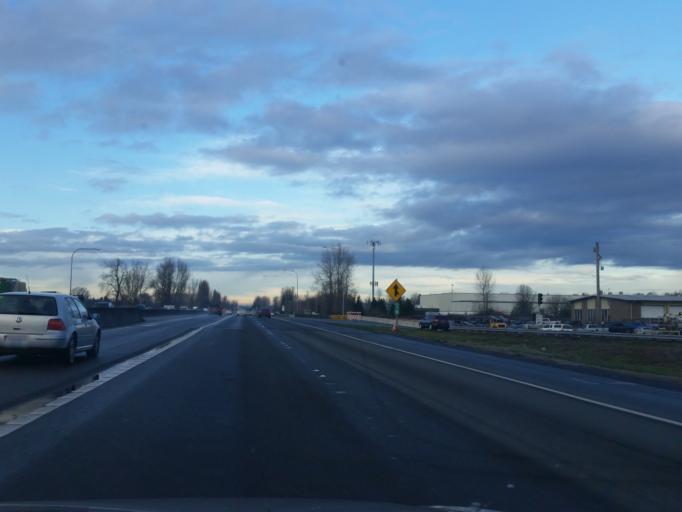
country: US
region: Washington
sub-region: King County
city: Kent
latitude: 47.3549
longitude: -122.2446
